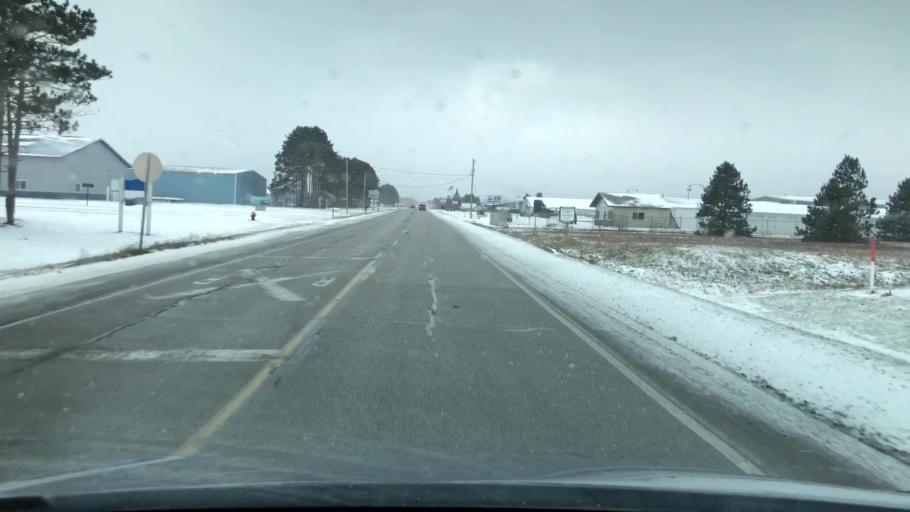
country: US
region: Michigan
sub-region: Wexford County
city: Cadillac
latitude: 44.2813
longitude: -85.4120
